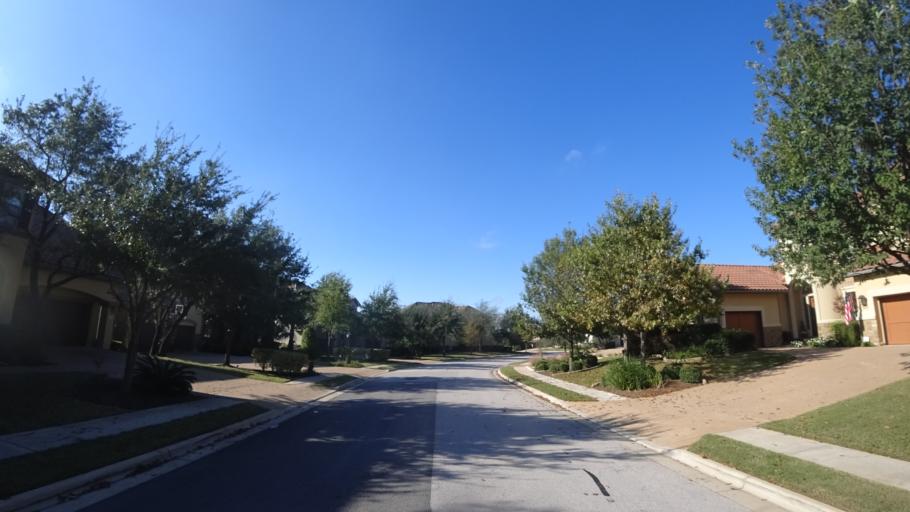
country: US
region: Texas
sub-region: Travis County
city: Bee Cave
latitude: 30.3505
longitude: -97.8947
